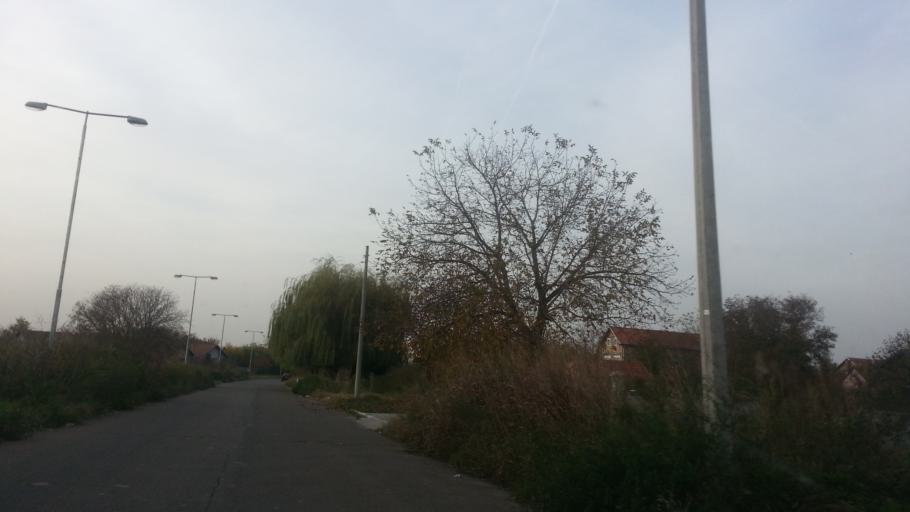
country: RS
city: Novi Banovci
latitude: 44.8933
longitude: 20.2837
